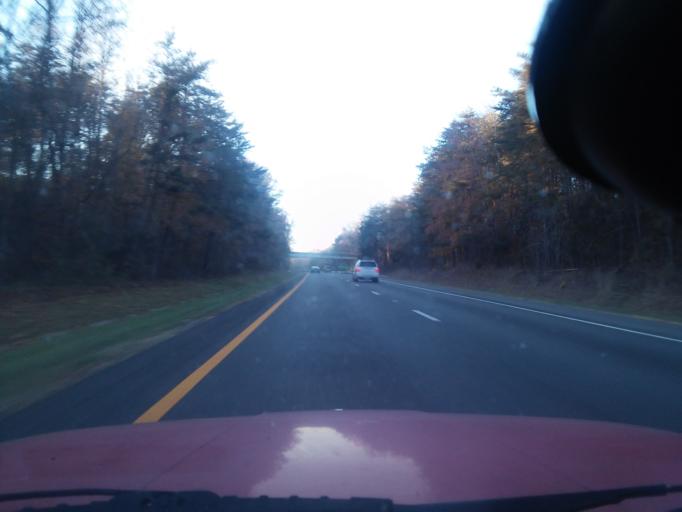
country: US
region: Virginia
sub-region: Goochland County
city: Goochland
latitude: 37.7422
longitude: -77.8356
